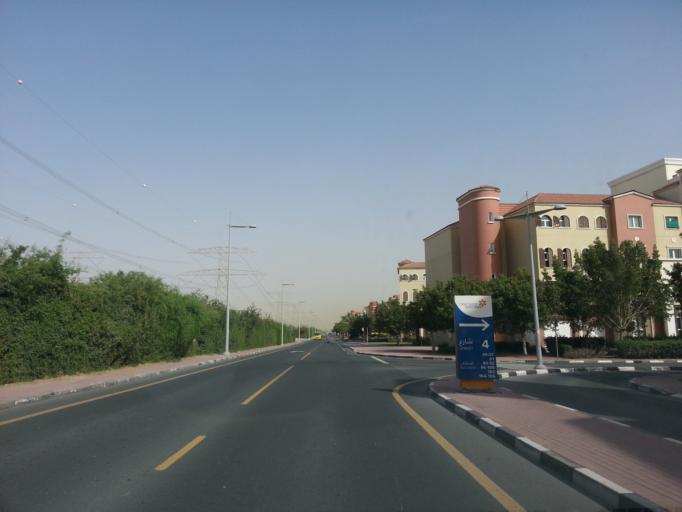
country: AE
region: Dubai
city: Dubai
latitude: 25.0452
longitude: 55.1412
